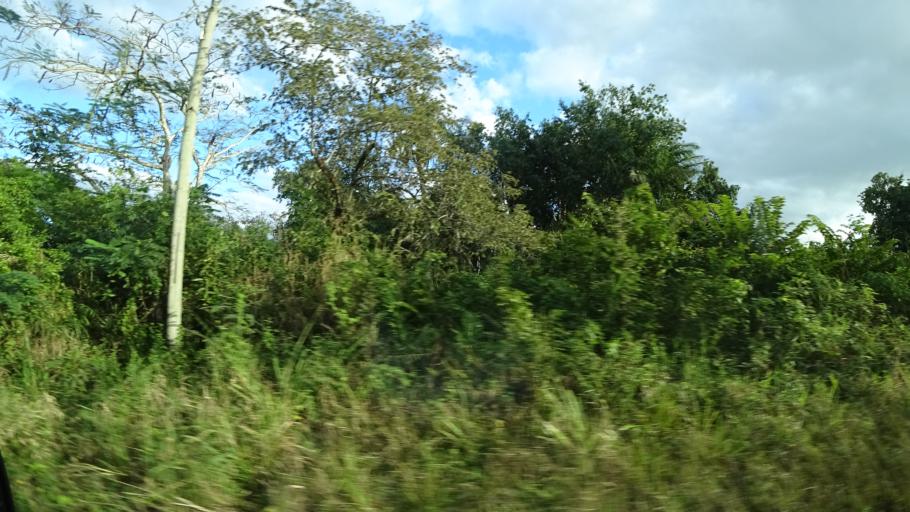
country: BZ
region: Belize
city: Belize City
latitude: 17.5695
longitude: -88.3996
